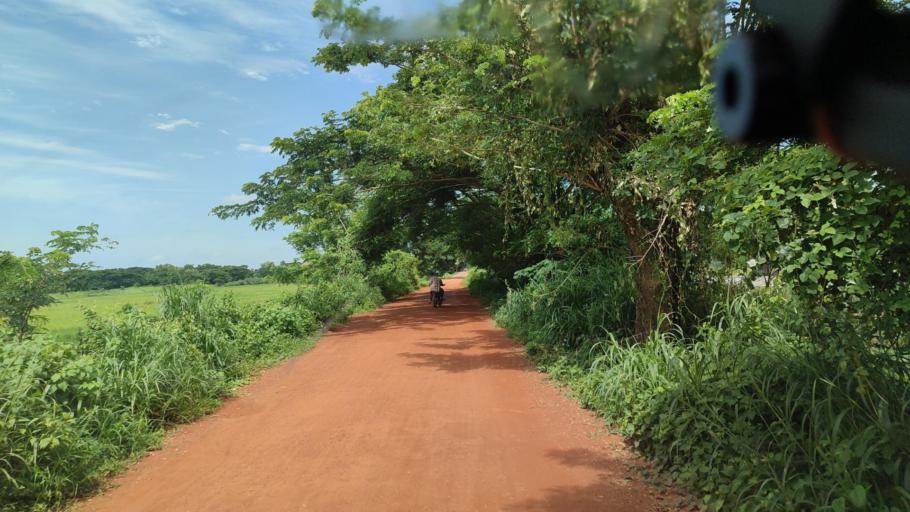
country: MM
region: Ayeyarwady
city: Hinthada
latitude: 17.6870
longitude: 95.4836
